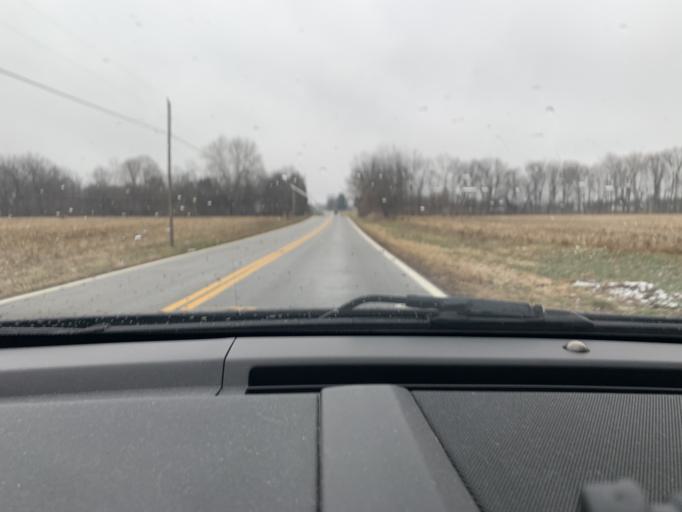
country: US
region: Ohio
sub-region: Ross County
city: Kingston
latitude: 39.4301
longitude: -82.9202
